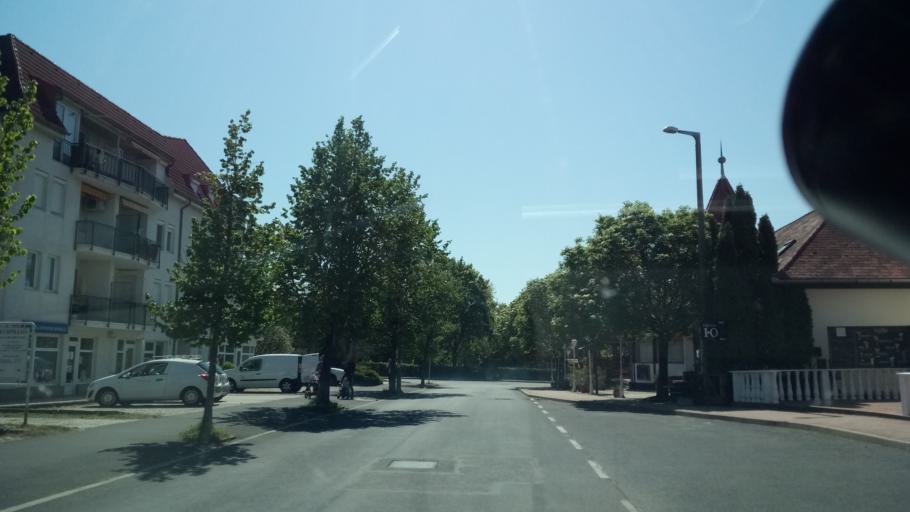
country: HU
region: Zala
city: Heviz
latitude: 46.7823
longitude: 17.1865
